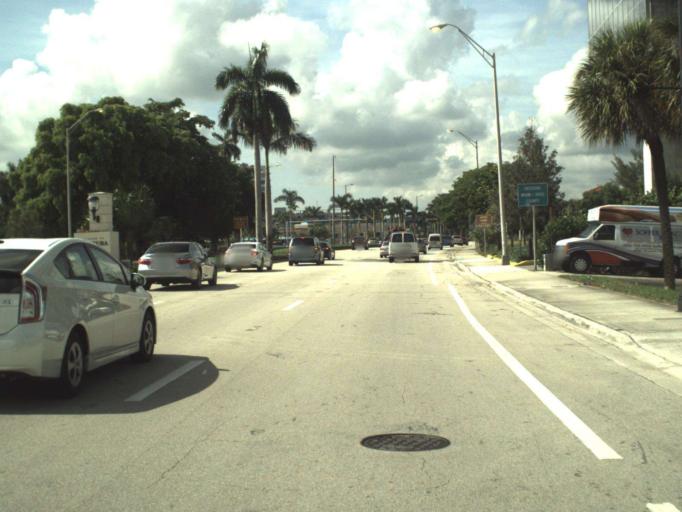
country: US
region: Florida
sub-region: Broward County
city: Hallandale Beach
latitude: 25.9749
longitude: -80.1423
